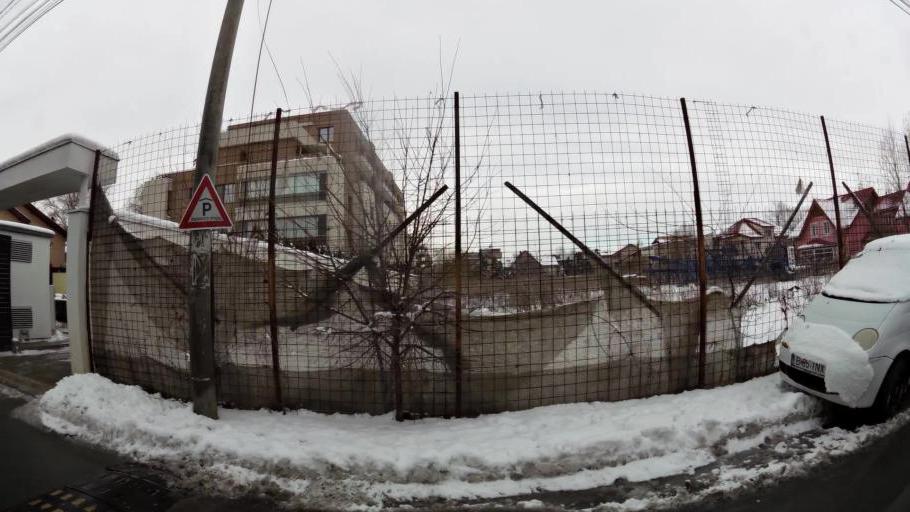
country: RO
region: Ilfov
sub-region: Comuna Tunari
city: Tunari
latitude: 44.5127
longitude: 26.1143
